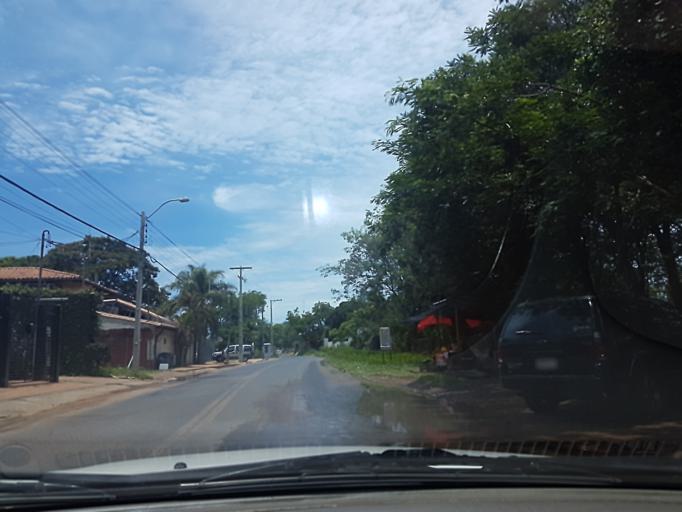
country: PY
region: Central
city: San Lorenzo
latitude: -25.2546
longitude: -57.5055
